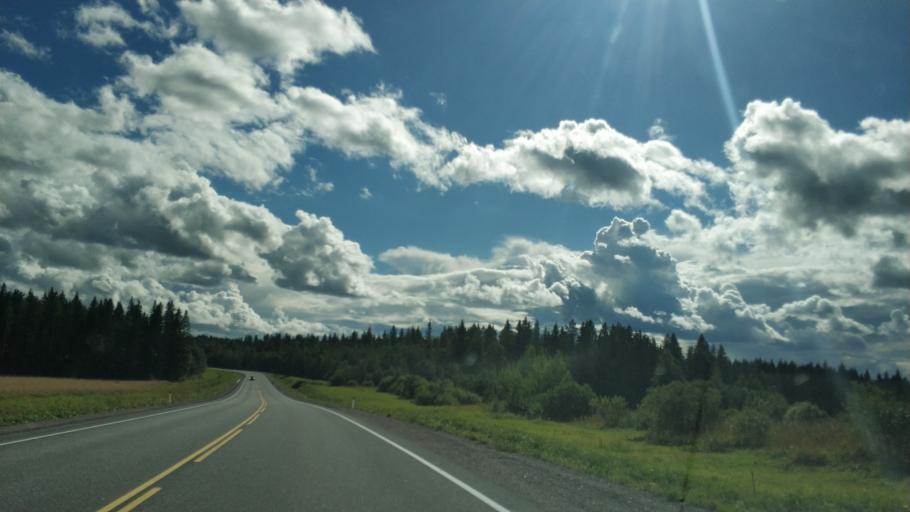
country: RU
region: Republic of Karelia
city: Ruskeala
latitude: 61.8816
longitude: 30.6435
